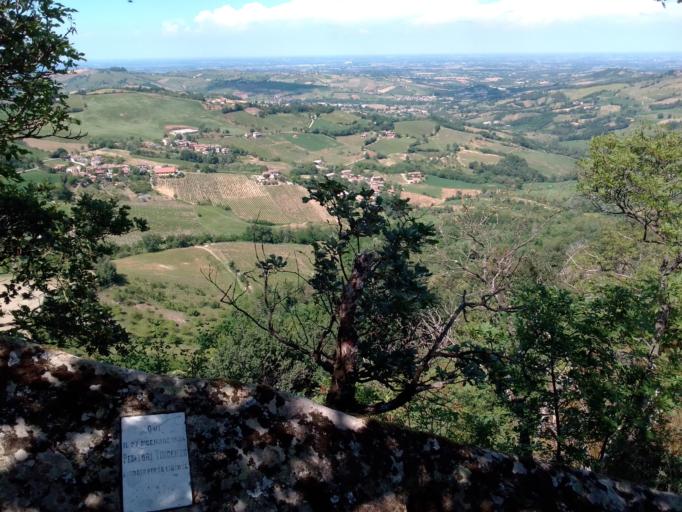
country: IT
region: Emilia-Romagna
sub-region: Provincia di Piacenza
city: Pianello Val Tidone
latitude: 44.9147
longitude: 9.3952
